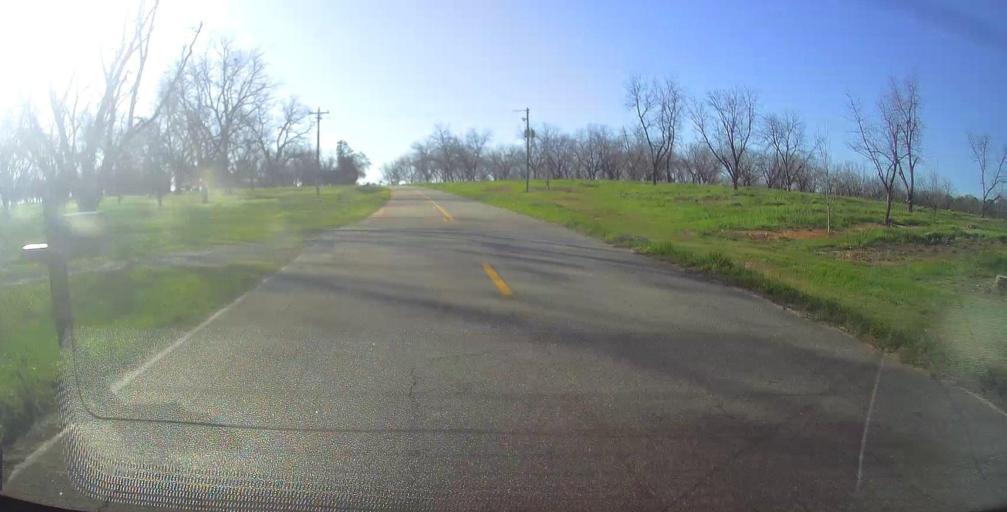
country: US
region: Georgia
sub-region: Houston County
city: Perry
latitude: 32.3668
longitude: -83.6814
